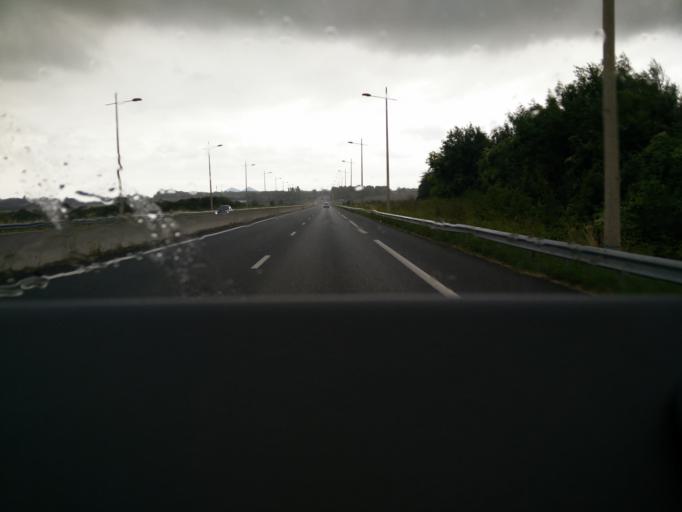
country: FR
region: Nord-Pas-de-Calais
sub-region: Departement du Pas-de-Calais
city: Sains-en-Gohelle
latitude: 50.4353
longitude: 2.6874
